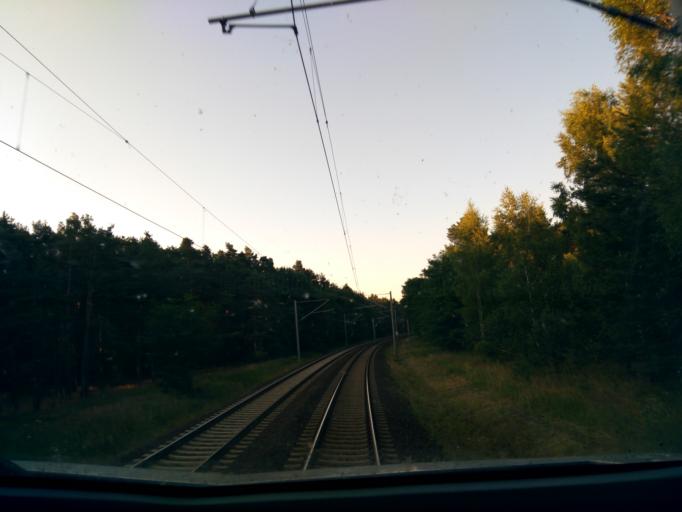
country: DE
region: Brandenburg
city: Bestensee
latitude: 52.2053
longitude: 13.6222
